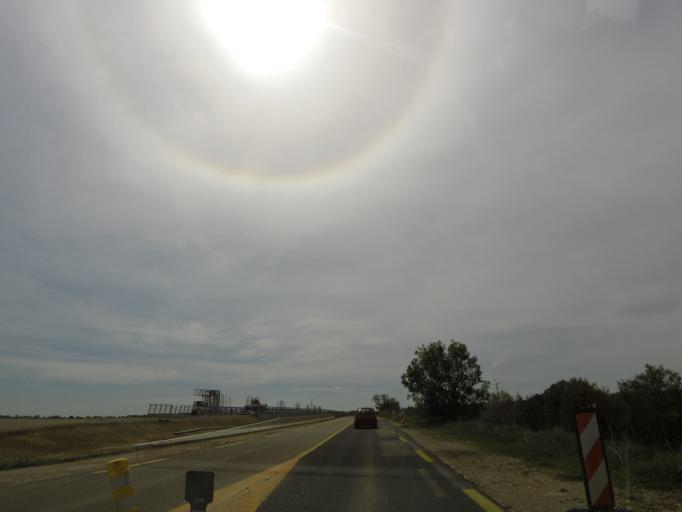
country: FR
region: Languedoc-Roussillon
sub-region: Departement de l'Herault
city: La Grande-Motte
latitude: 43.5865
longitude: 4.1043
